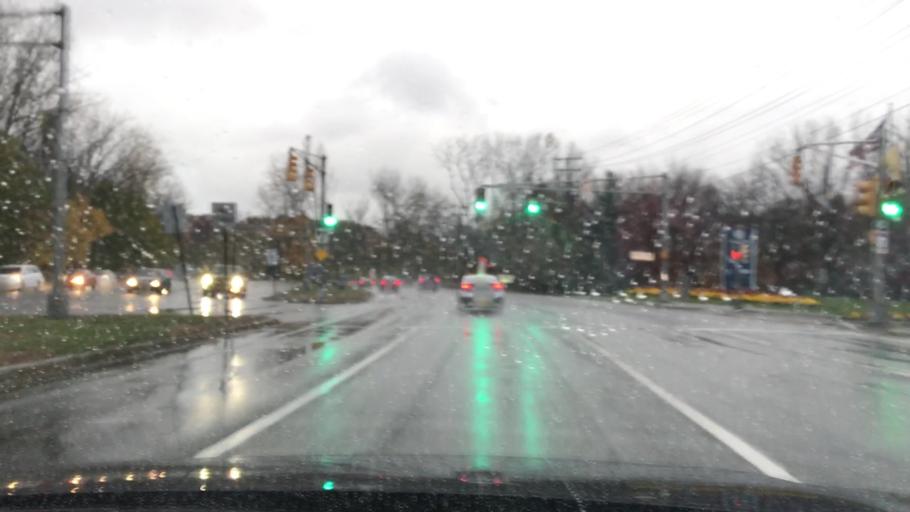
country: US
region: New Jersey
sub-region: Bergen County
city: Ridgefield Park
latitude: 40.8716
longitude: -74.0066
